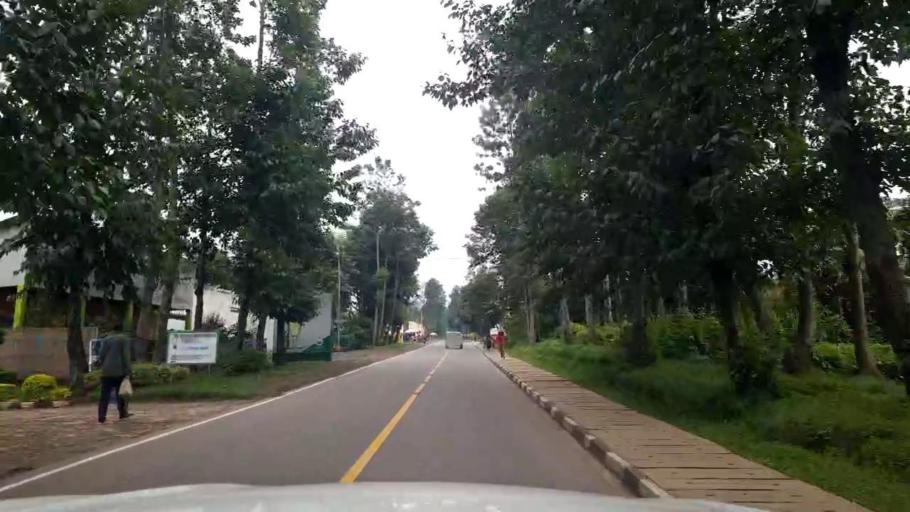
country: RW
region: Northern Province
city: Musanze
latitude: -1.4608
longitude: 29.6132
